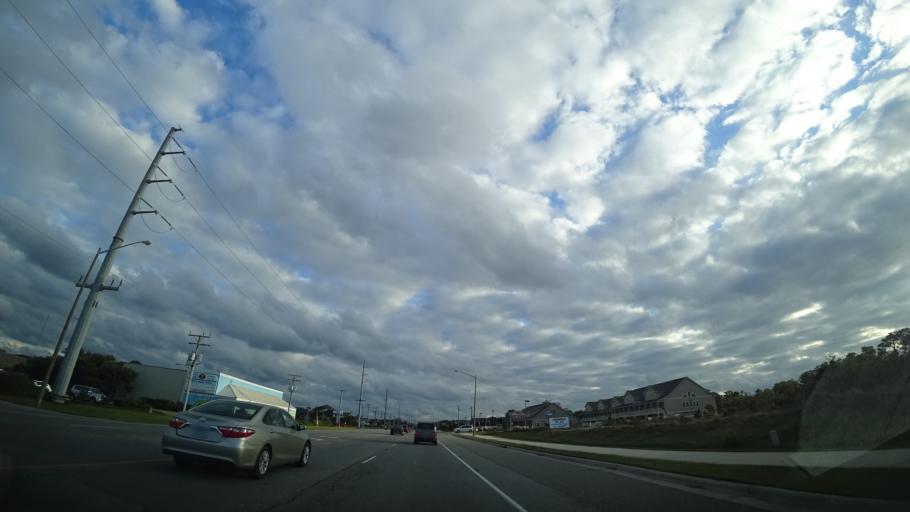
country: US
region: North Carolina
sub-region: Dare County
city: Nags Head
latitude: 35.9874
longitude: -75.6456
